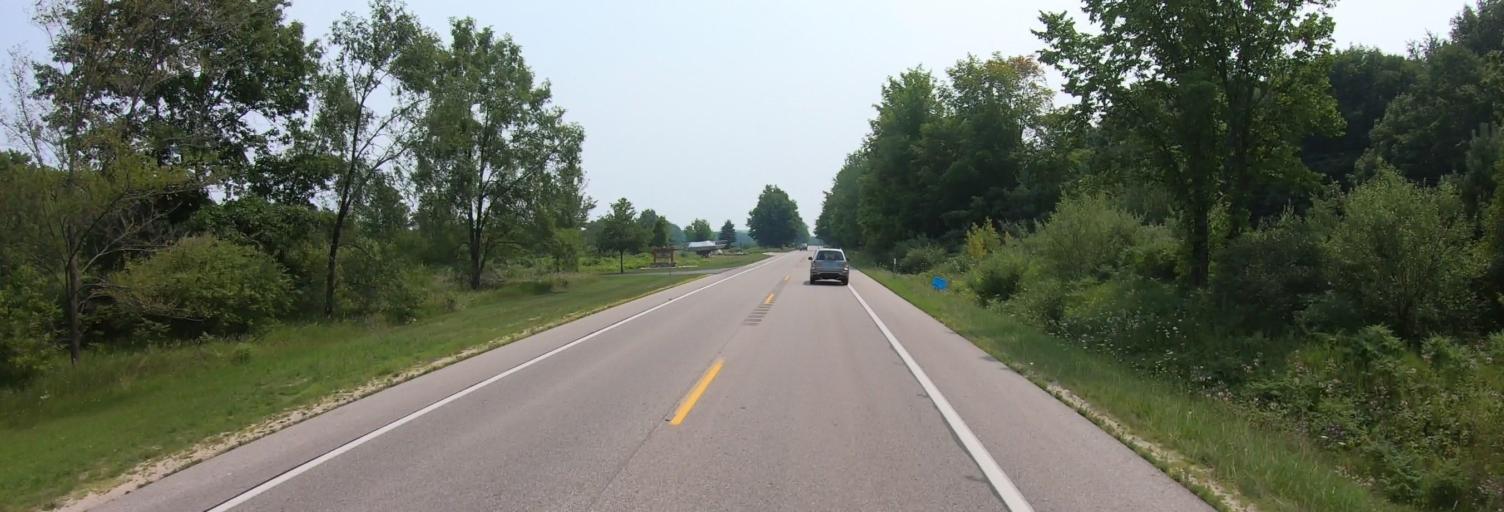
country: US
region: Michigan
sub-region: Leelanau County
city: Leland
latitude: 45.0782
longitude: -85.5919
